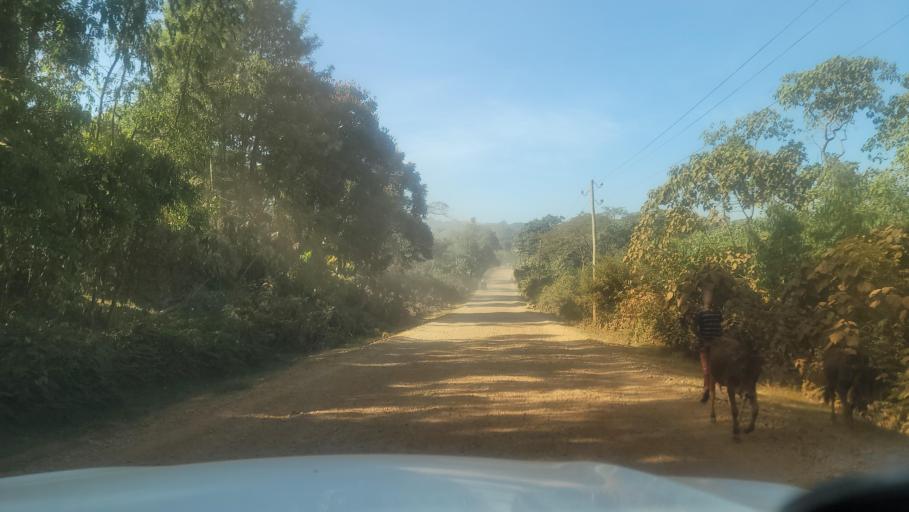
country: ET
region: Oromiya
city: Agaro
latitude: 7.8416
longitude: 36.5598
